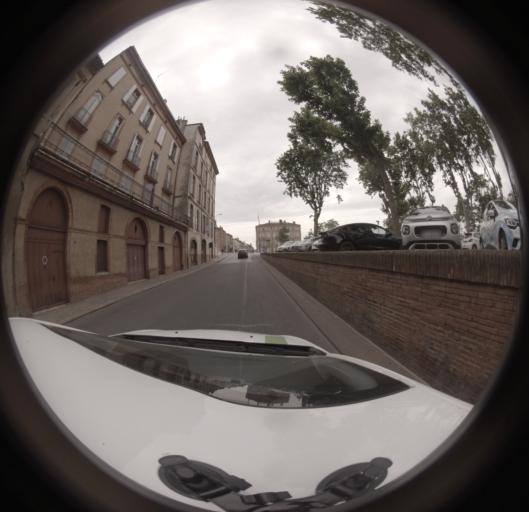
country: FR
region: Midi-Pyrenees
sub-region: Departement du Tarn-et-Garonne
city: Montauban
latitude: 44.0146
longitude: 1.3543
